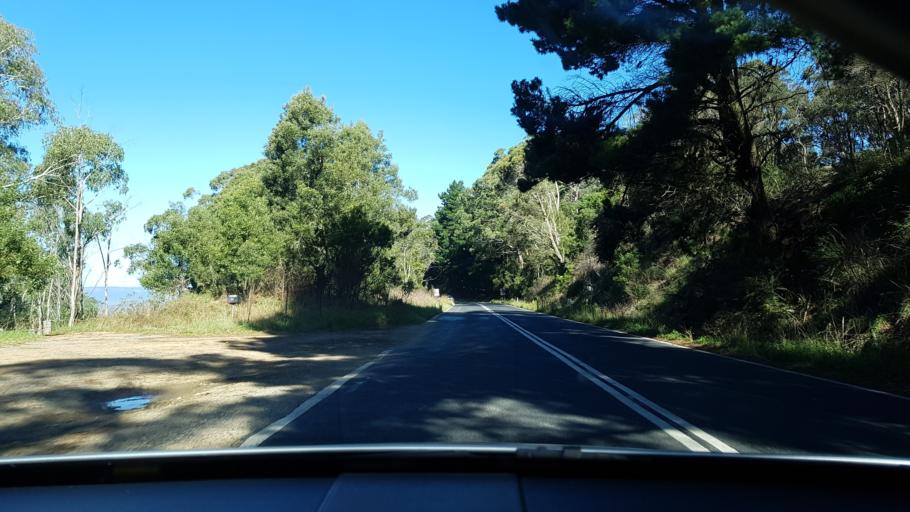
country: AU
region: New South Wales
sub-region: Lithgow
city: Bowenfels
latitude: -33.6493
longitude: 150.0502
